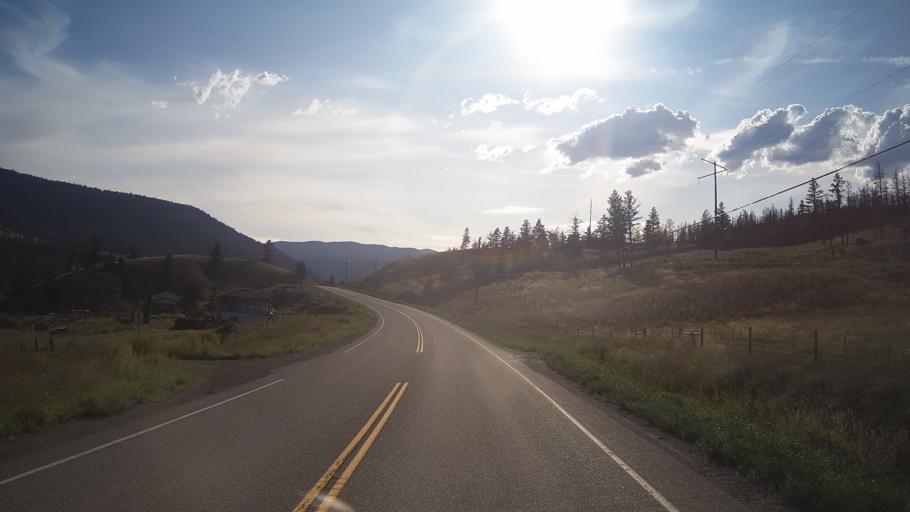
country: CA
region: British Columbia
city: Cache Creek
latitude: 50.8878
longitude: -121.4519
